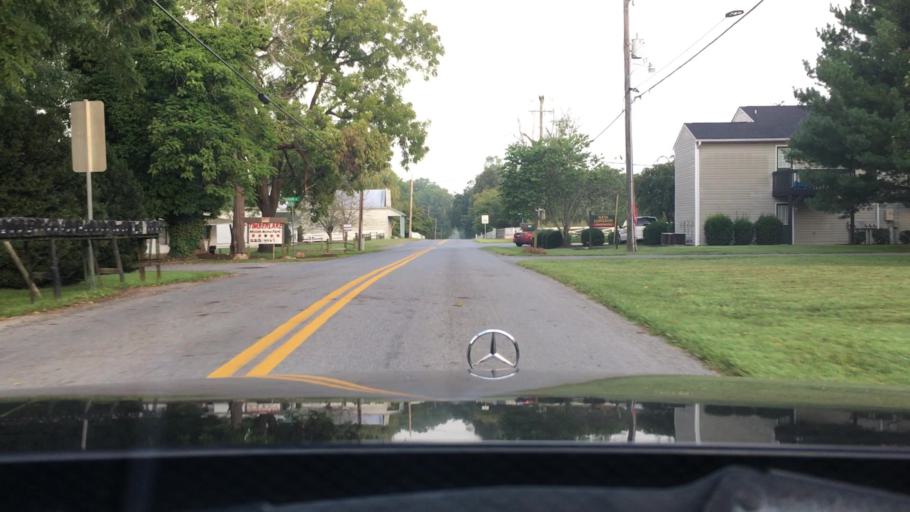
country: US
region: Virginia
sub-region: Campbell County
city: Timberlake
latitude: 37.3019
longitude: -79.2810
